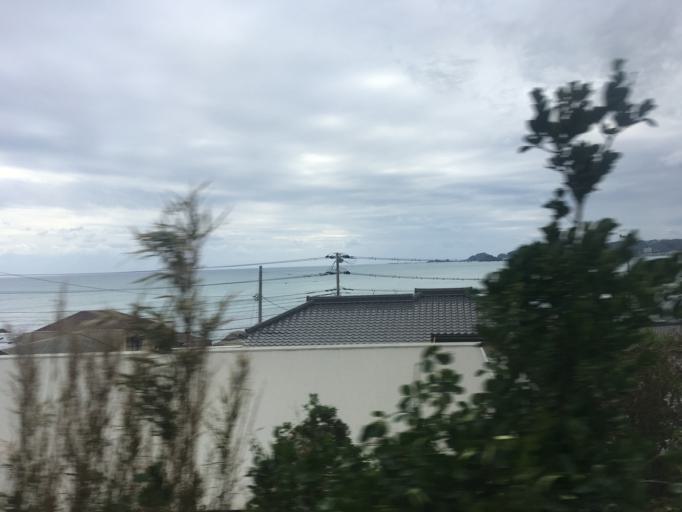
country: JP
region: Chiba
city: Kawaguchi
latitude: 35.1224
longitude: 140.1365
